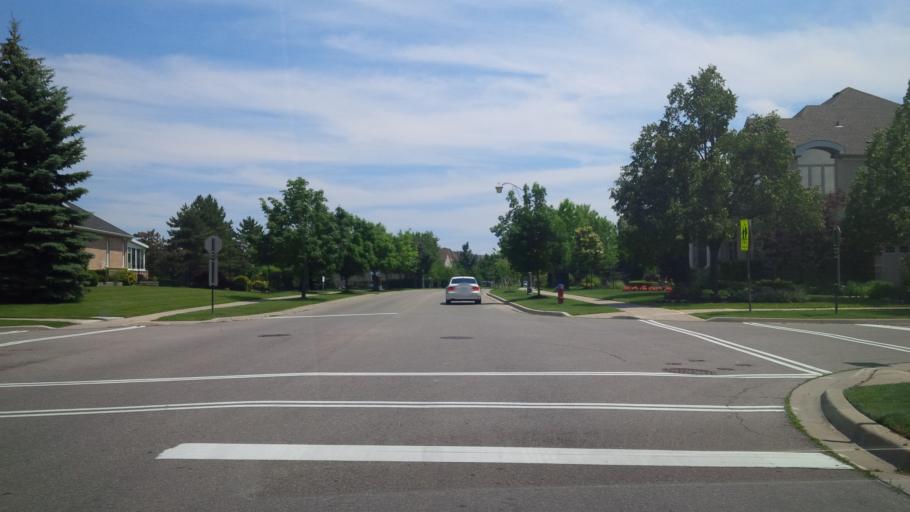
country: CA
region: Ontario
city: Burlington
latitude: 43.3982
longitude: -79.8047
